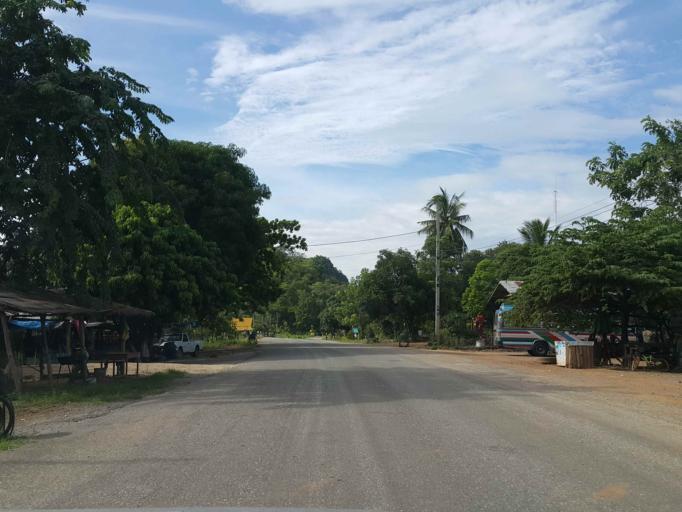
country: TH
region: Sukhothai
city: Thung Saliam
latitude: 17.2678
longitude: 99.5345
